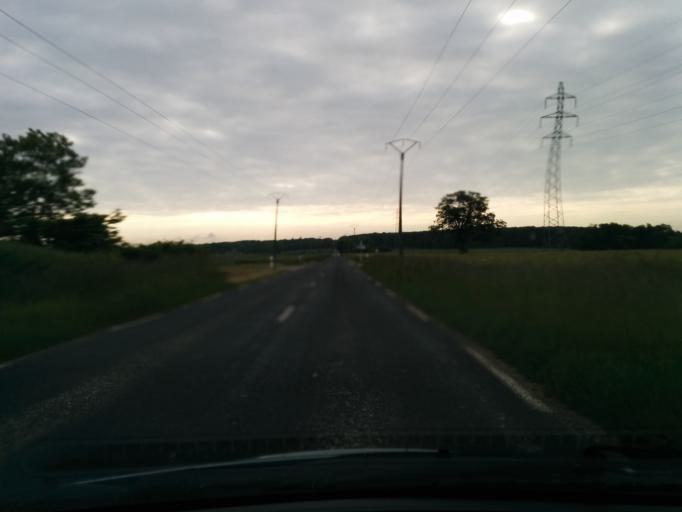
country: FR
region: Ile-de-France
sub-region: Departement des Yvelines
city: Limetz-Villez
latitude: 49.0943
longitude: 1.5588
